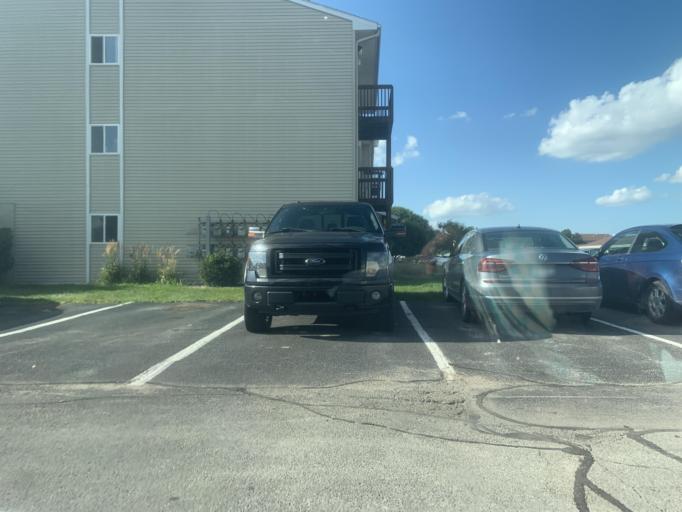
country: US
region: Nebraska
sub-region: Sarpy County
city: Chalco
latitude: 41.1772
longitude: -96.1459
